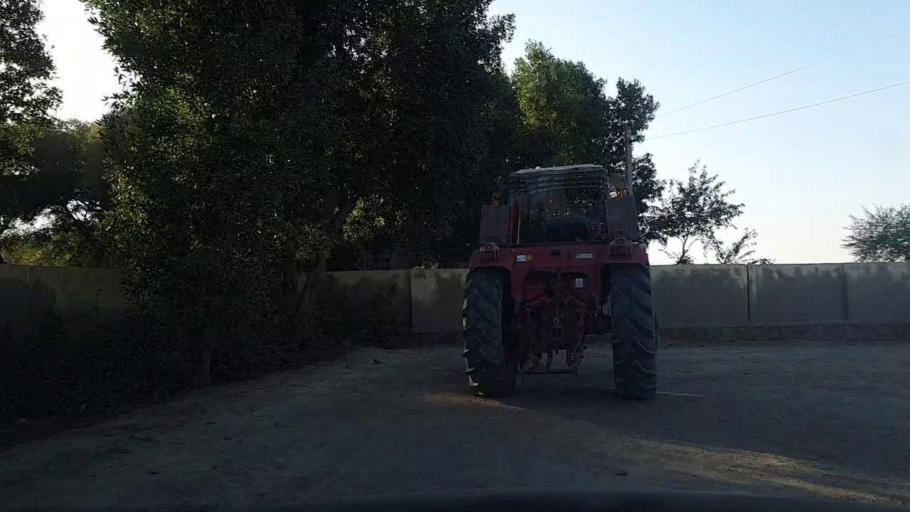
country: PK
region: Sindh
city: Mirpur Batoro
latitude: 24.7068
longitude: 68.3203
